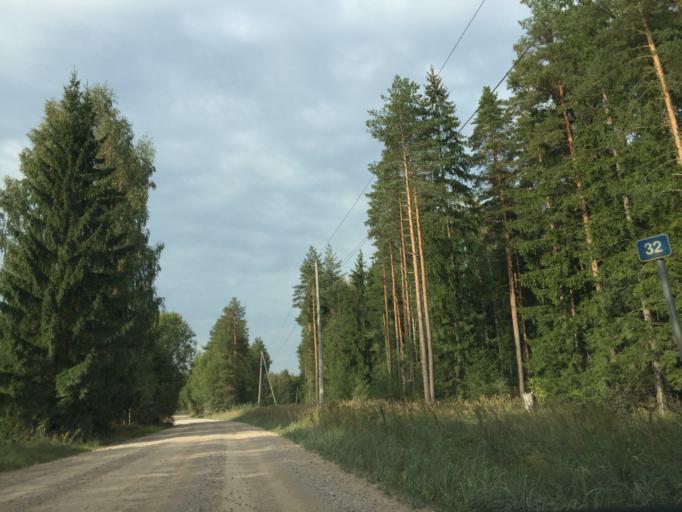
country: LV
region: Ikskile
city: Ikskile
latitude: 56.8039
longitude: 24.4406
